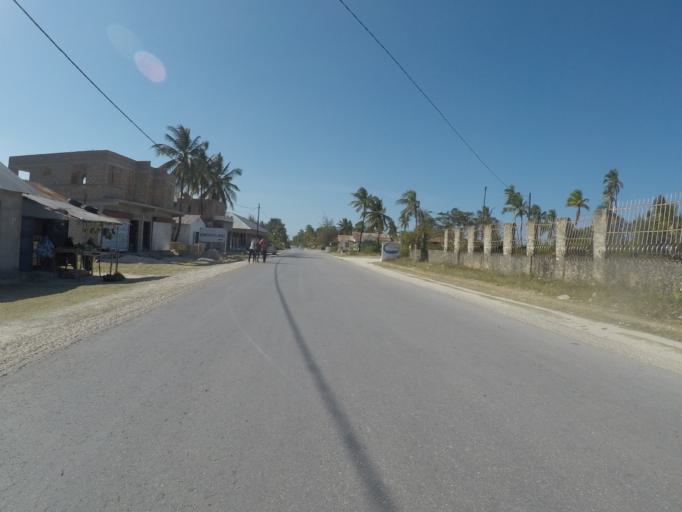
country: TZ
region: Zanzibar Central/South
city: Nganane
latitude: -6.2614
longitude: 39.5327
